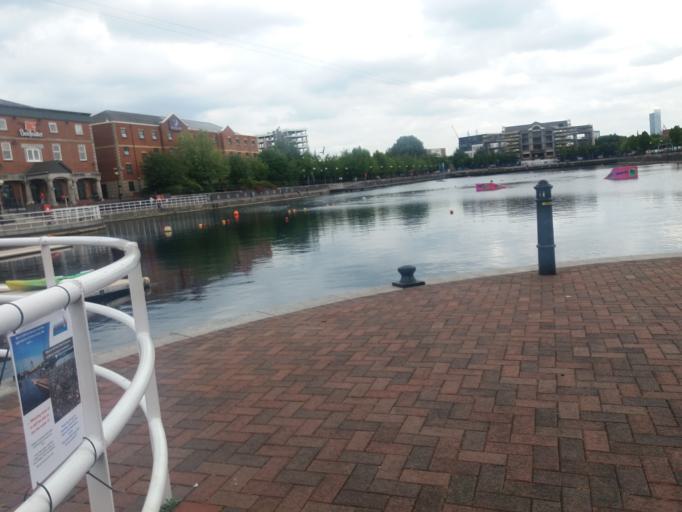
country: GB
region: England
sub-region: City and Borough of Salford
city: Salford
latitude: 53.4705
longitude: -2.2885
